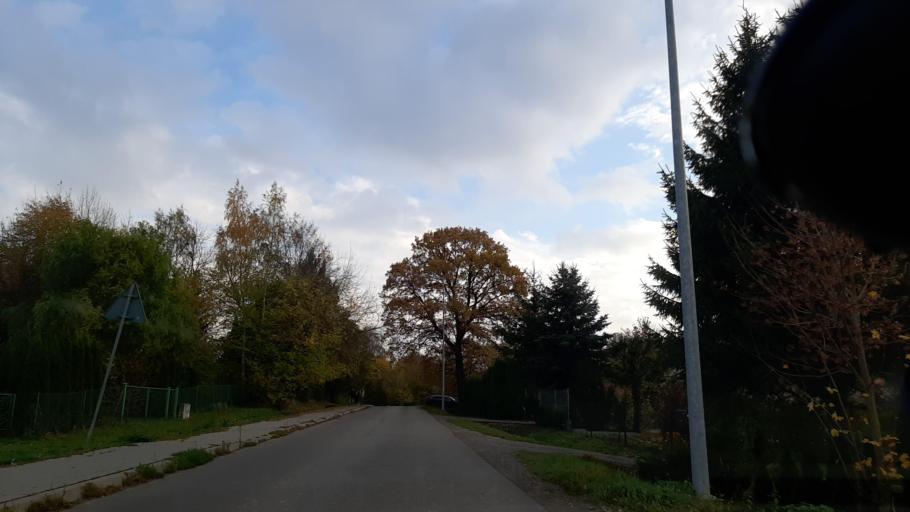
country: PL
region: Lublin Voivodeship
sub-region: Powiat pulawski
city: Naleczow
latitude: 51.3136
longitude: 22.2140
